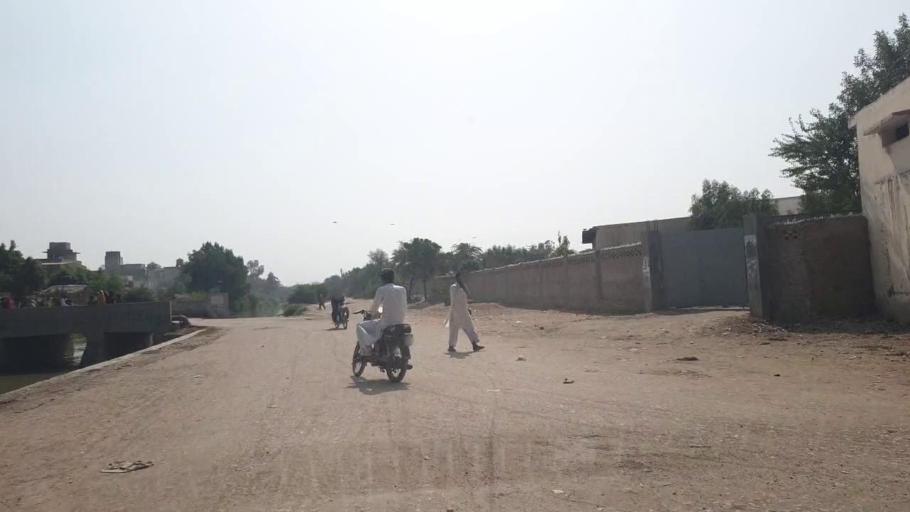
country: PK
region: Sindh
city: Badin
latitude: 24.6547
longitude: 68.8423
